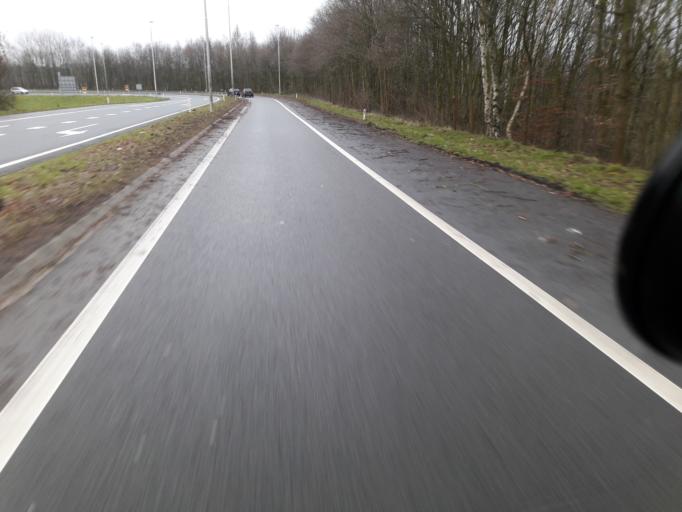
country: NL
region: Overijssel
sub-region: Gemeente Hengelo
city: Hengelo
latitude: 52.2759
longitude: 6.8332
